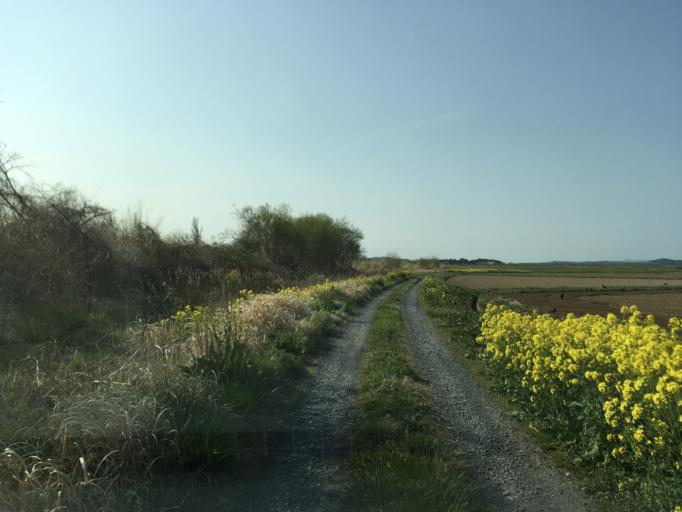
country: JP
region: Miyagi
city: Wakuya
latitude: 38.7103
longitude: 141.2718
